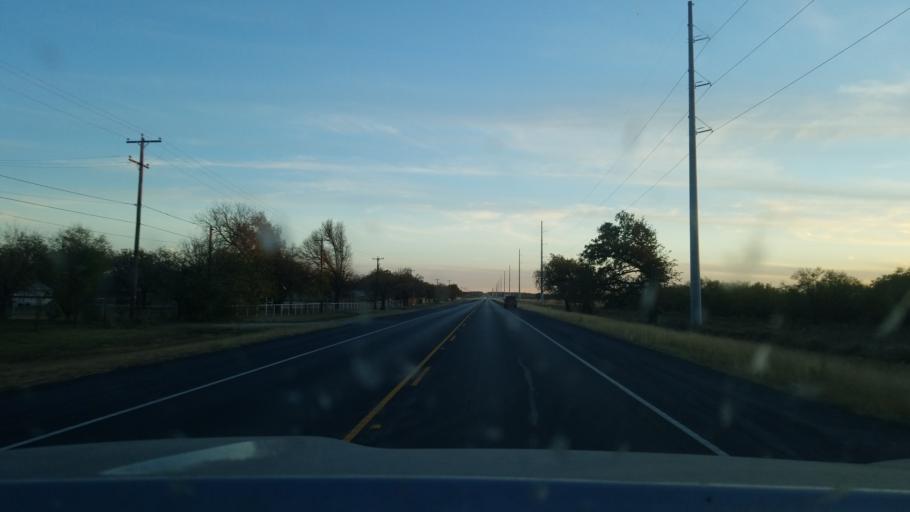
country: US
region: Texas
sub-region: Stephens County
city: Breckenridge
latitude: 32.7213
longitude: -98.9025
